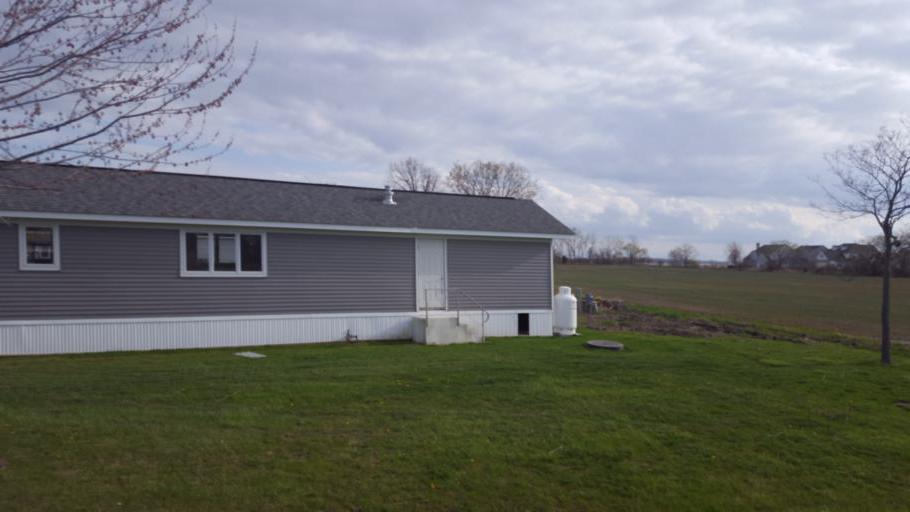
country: US
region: Ohio
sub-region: Erie County
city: Sandusky
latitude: 41.5081
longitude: -82.7826
